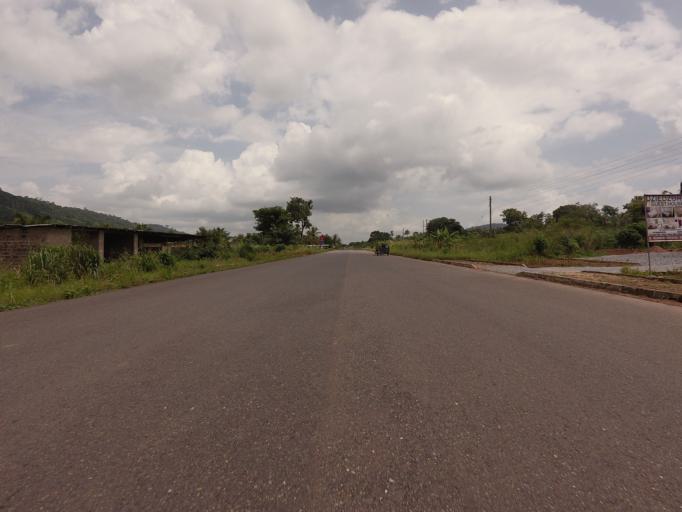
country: GH
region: Volta
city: Ho
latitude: 6.5053
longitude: 0.2096
